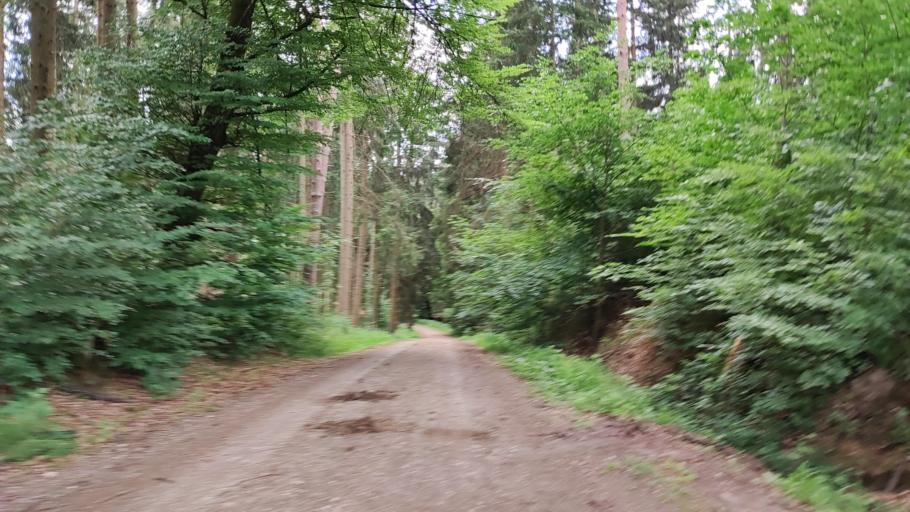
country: DE
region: Bavaria
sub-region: Swabia
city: Adelsried
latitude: 48.4105
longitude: 10.7095
